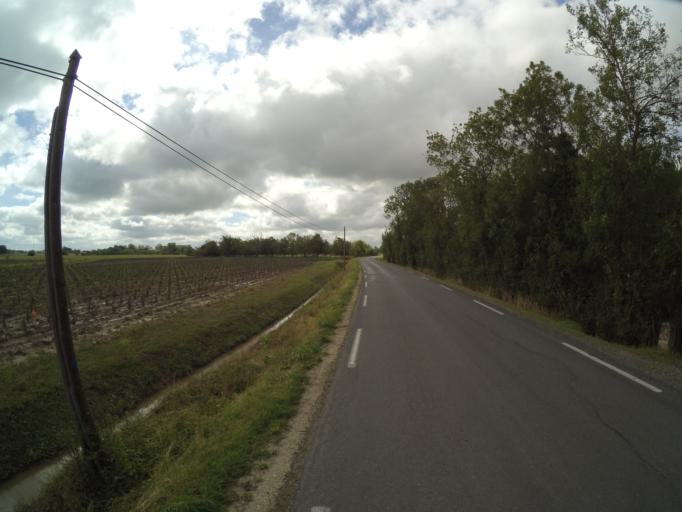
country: FR
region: Aquitaine
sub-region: Departement de la Gironde
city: Macau
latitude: 45.0021
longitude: -0.6023
